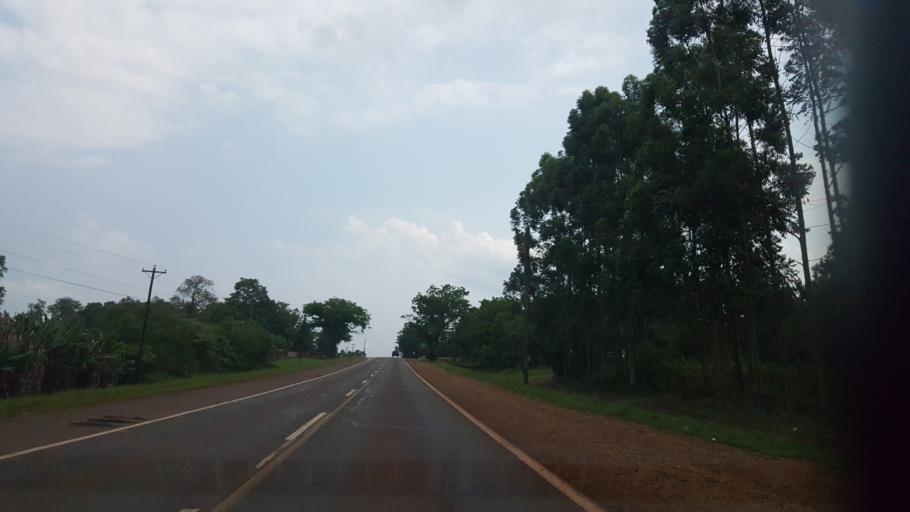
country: AR
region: Misiones
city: Jardin America
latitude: -27.0666
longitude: -55.2669
